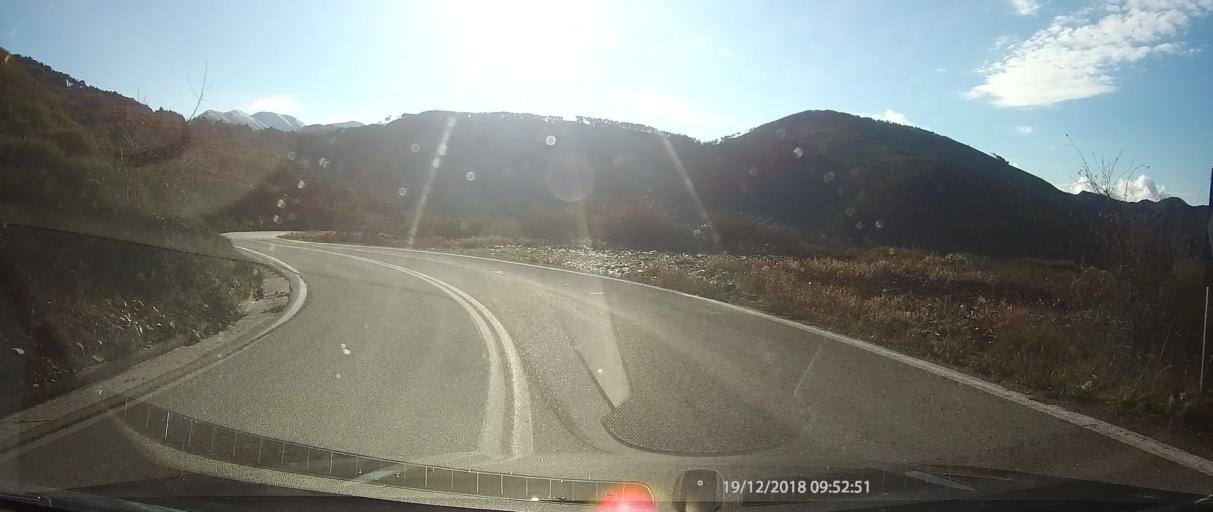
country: GR
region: Peloponnese
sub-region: Nomos Messinias
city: Paralia Vergas
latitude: 37.0709
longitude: 22.2550
